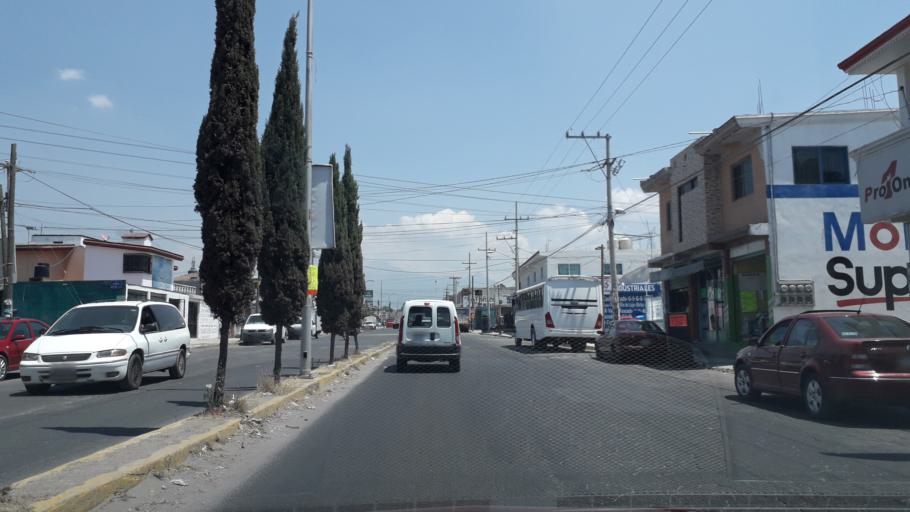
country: MX
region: Puebla
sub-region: Puebla
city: Primero de Mayo
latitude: 19.0718
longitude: -98.1153
